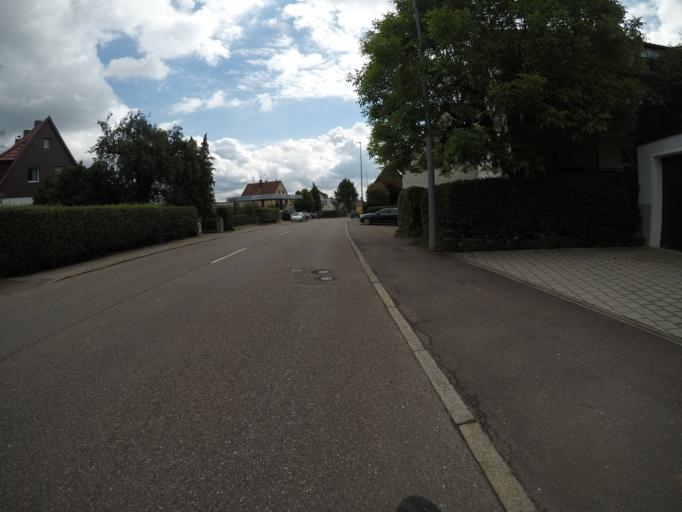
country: DE
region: Baden-Wuerttemberg
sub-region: Regierungsbezirk Stuttgart
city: Esslingen
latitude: 48.7192
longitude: 9.3137
